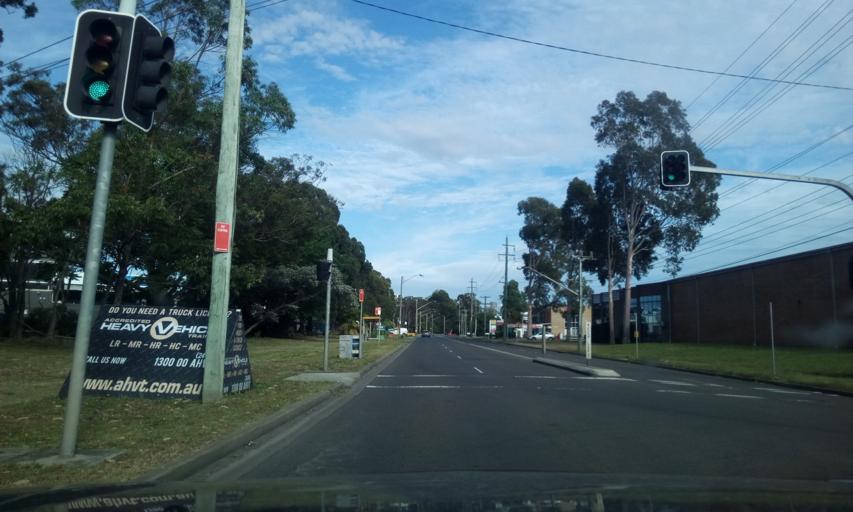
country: AU
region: New South Wales
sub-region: Fairfield
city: Liverpool
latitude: -33.9378
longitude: 150.9387
